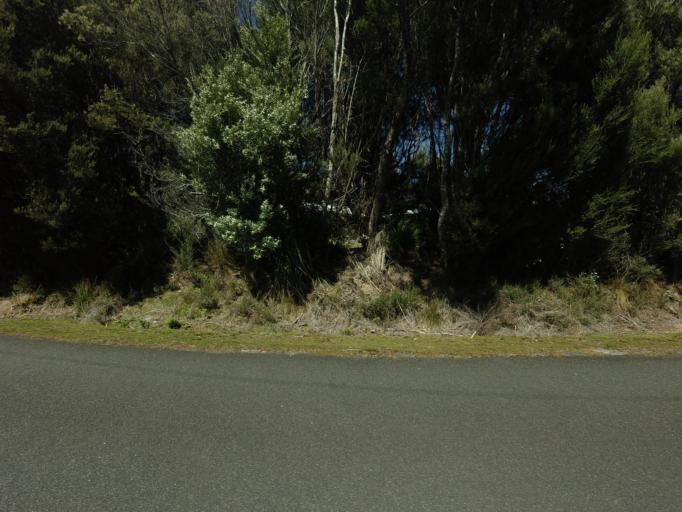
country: AU
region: Tasmania
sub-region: West Coast
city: Queenstown
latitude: -42.7662
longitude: 146.0456
